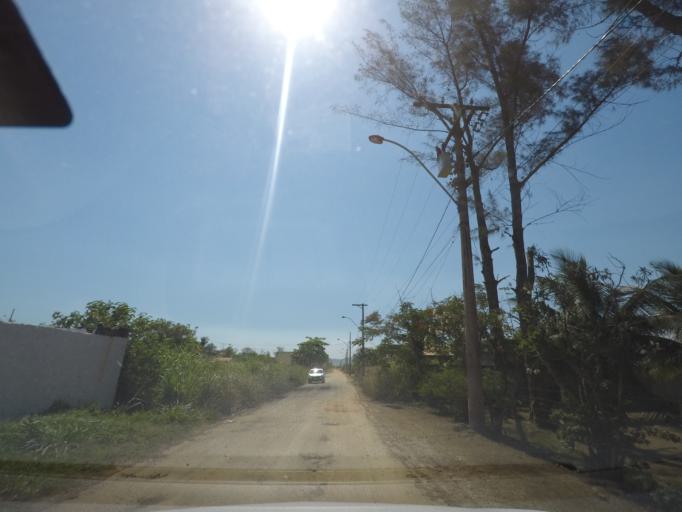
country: BR
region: Rio de Janeiro
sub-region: Marica
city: Marica
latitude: -22.9728
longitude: -42.9227
